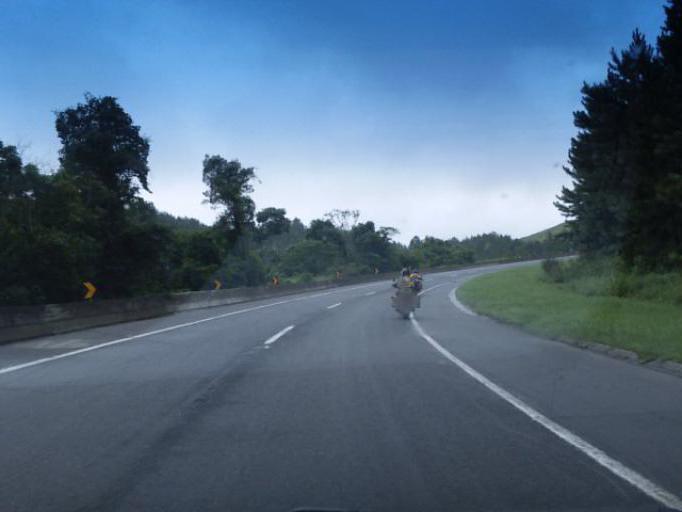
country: BR
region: Sao Paulo
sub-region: Cajati
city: Cajati
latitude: -24.9771
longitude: -48.5045
